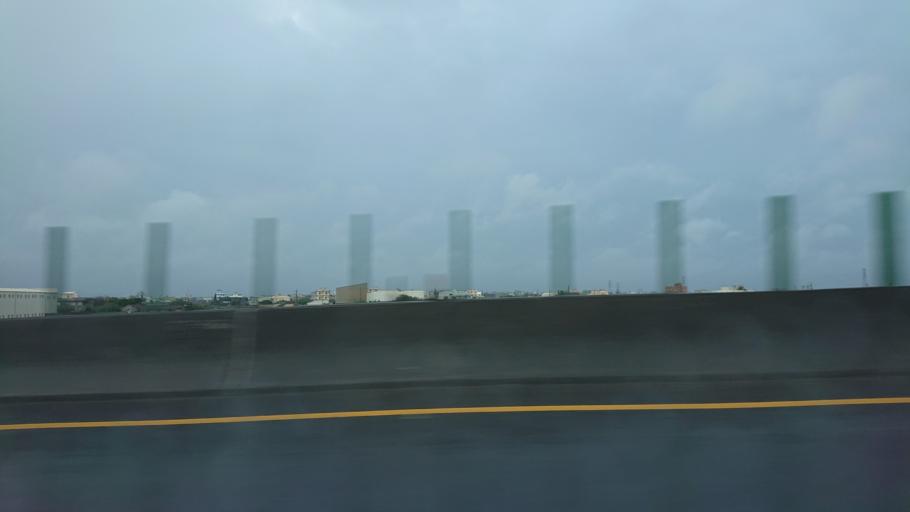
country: TW
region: Taiwan
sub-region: Changhua
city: Chang-hua
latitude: 24.1359
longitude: 120.4419
